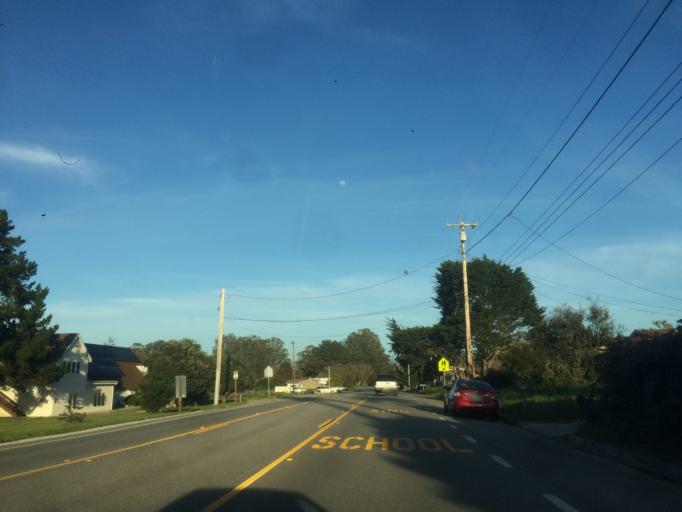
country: US
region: California
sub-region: San Luis Obispo County
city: Los Osos
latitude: 35.3126
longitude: -120.8464
